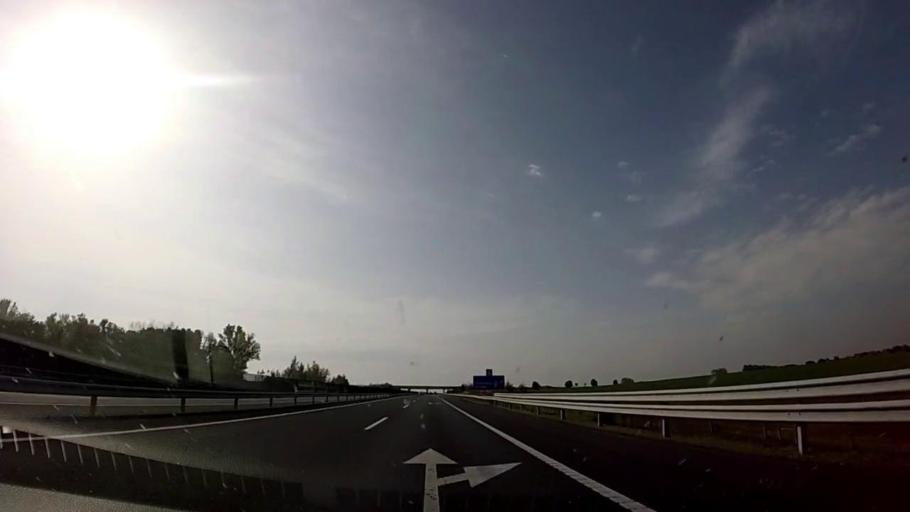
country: HU
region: Zala
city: Murakeresztur
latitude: 46.4615
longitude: 16.8902
